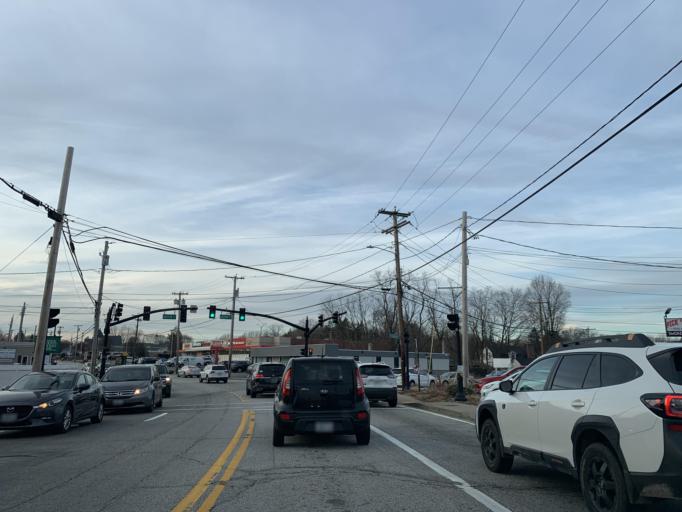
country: US
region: Rhode Island
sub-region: Providence County
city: Greenville
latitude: 41.8722
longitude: -71.5536
